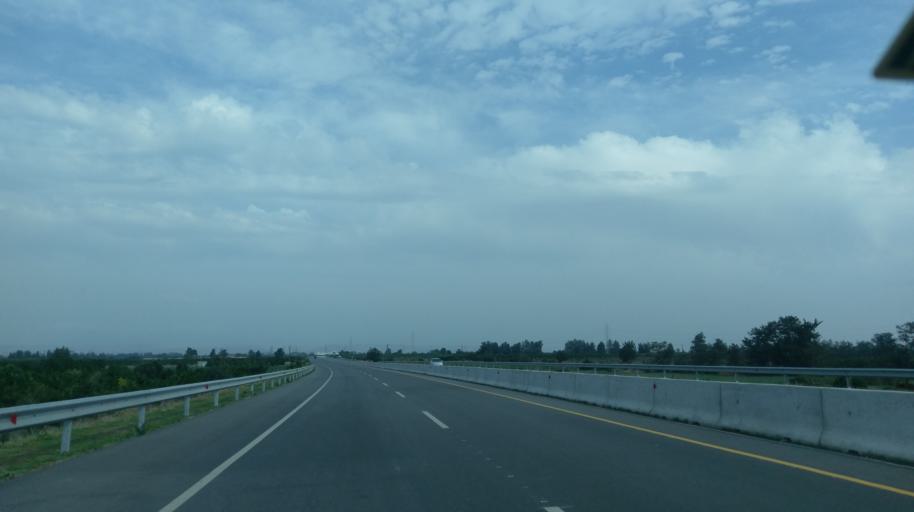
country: CY
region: Lefkosia
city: Morfou
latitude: 35.1748
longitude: 32.9617
